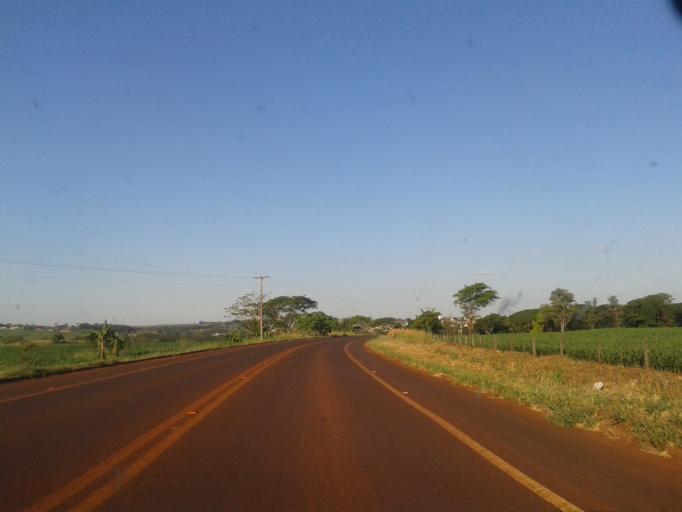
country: BR
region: Minas Gerais
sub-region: Capinopolis
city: Capinopolis
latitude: -18.6835
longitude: -49.5947
